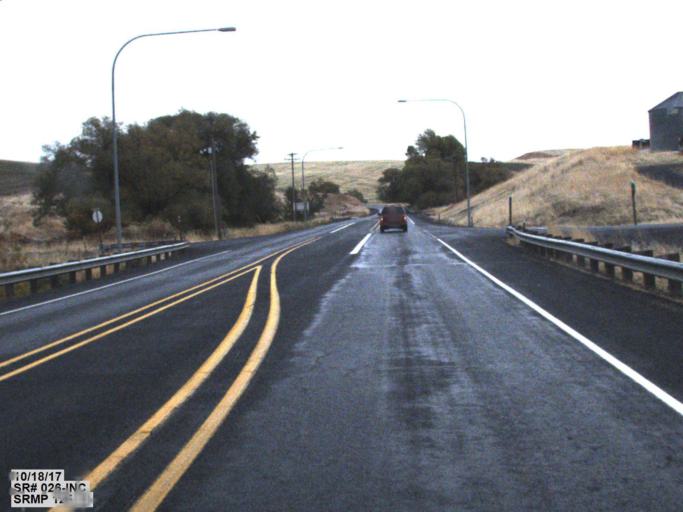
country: US
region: Washington
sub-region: Whitman County
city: Colfax
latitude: 46.8329
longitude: -117.5063
